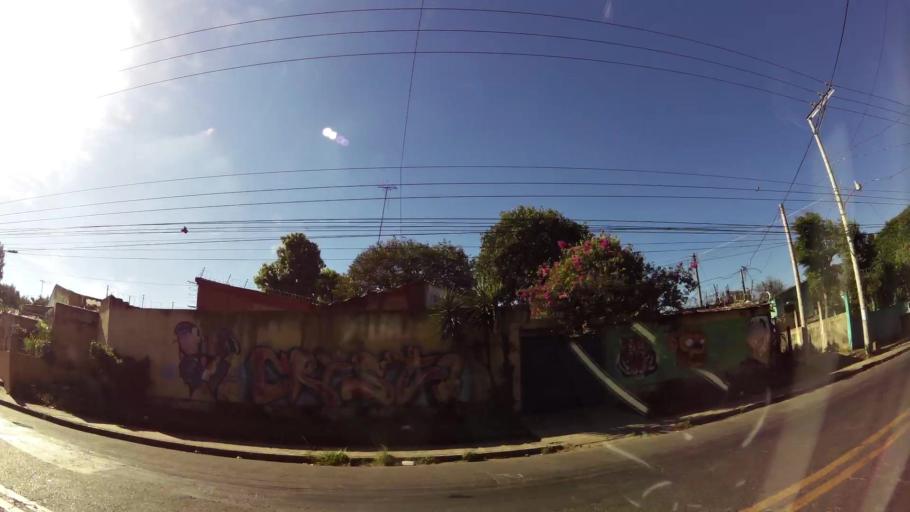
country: SV
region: Santa Ana
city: Santa Ana
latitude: 13.9808
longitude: -89.5655
